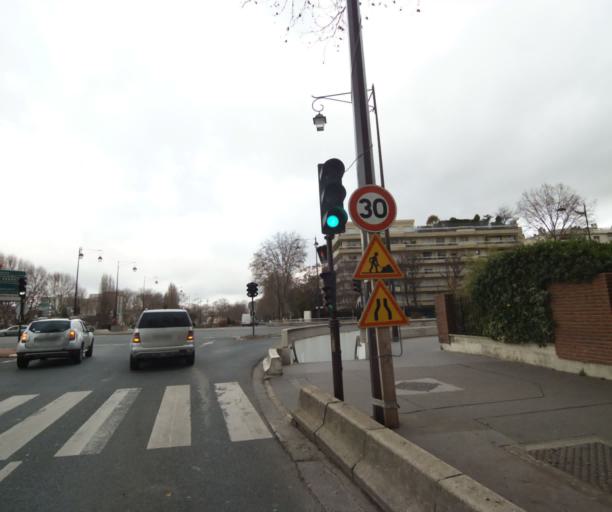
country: FR
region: Ile-de-France
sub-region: Departement des Hauts-de-Seine
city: Neuilly-sur-Seine
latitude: 48.8933
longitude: 2.2673
